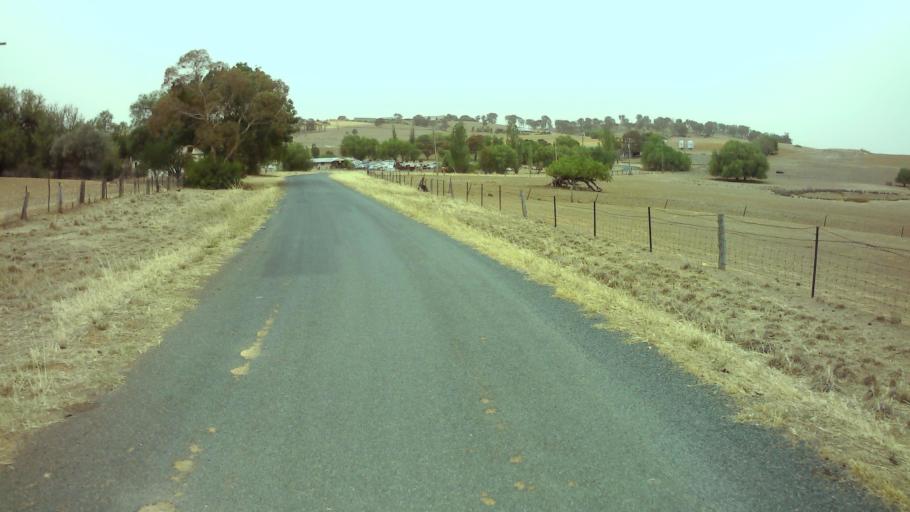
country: AU
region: New South Wales
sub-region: Weddin
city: Grenfell
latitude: -33.9046
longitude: 148.1696
